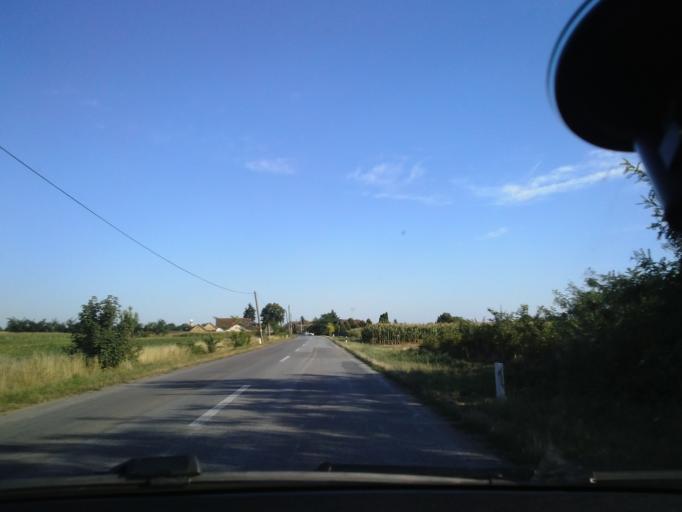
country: RS
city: Doroslovo
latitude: 45.5687
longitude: 19.1940
